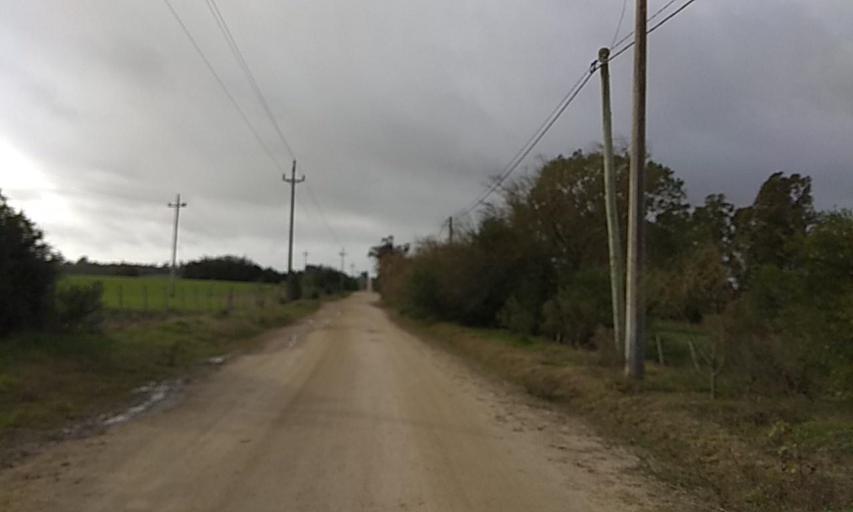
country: UY
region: Florida
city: Florida
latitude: -34.0577
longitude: -56.2219
